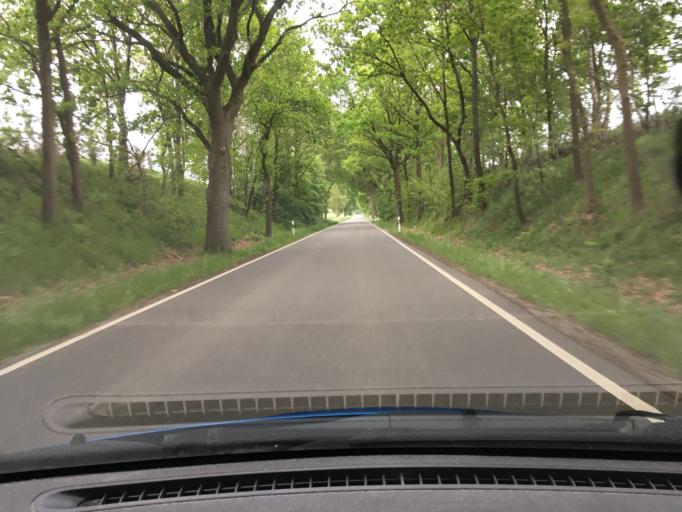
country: DE
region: Lower Saxony
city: Eyendorf
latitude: 53.1909
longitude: 10.1553
